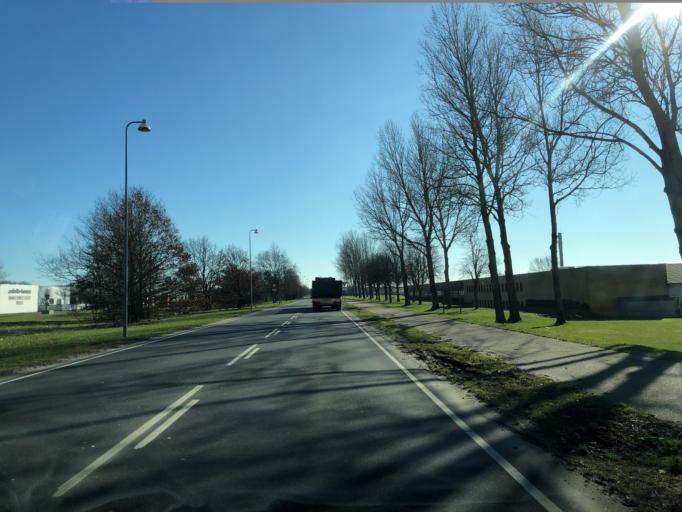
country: DK
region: Central Jutland
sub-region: Ikast-Brande Kommune
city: Ikast
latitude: 56.1306
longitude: 9.1672
